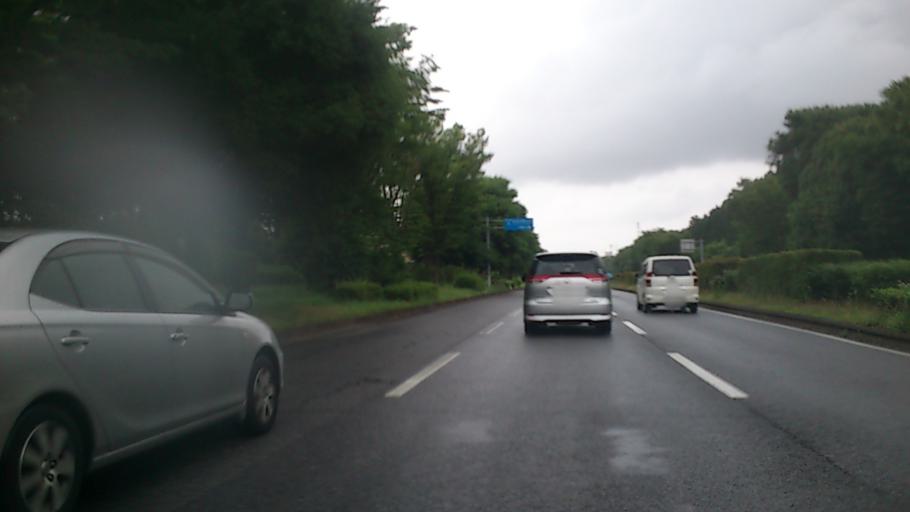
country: JP
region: Ibaraki
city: Naka
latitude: 36.0840
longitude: 140.1053
